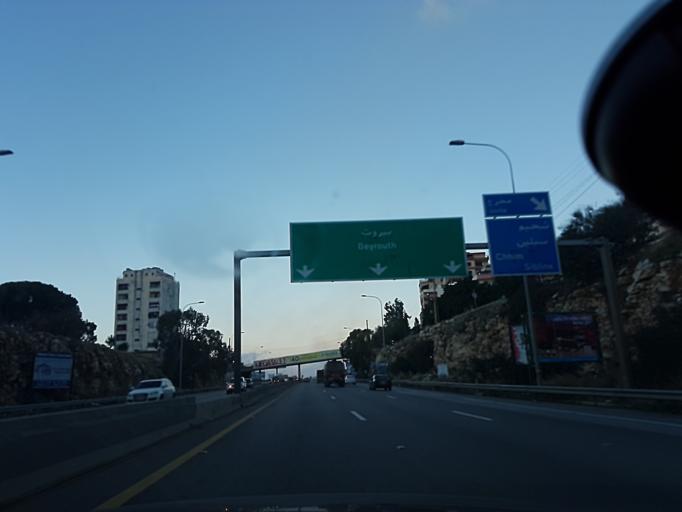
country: LB
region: Liban-Sud
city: Sidon
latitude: 33.6197
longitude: 35.4028
